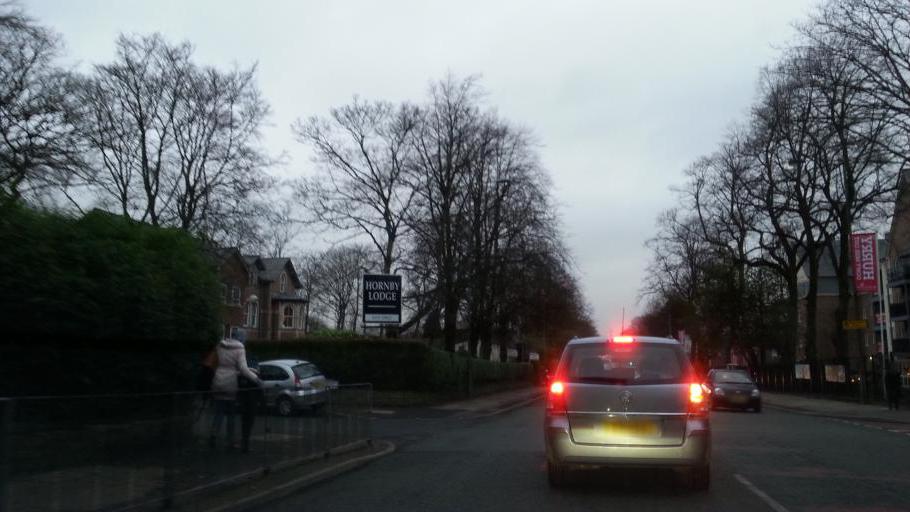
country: GB
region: England
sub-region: Borough of Bury
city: Prestwich
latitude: 53.5260
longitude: -2.2787
